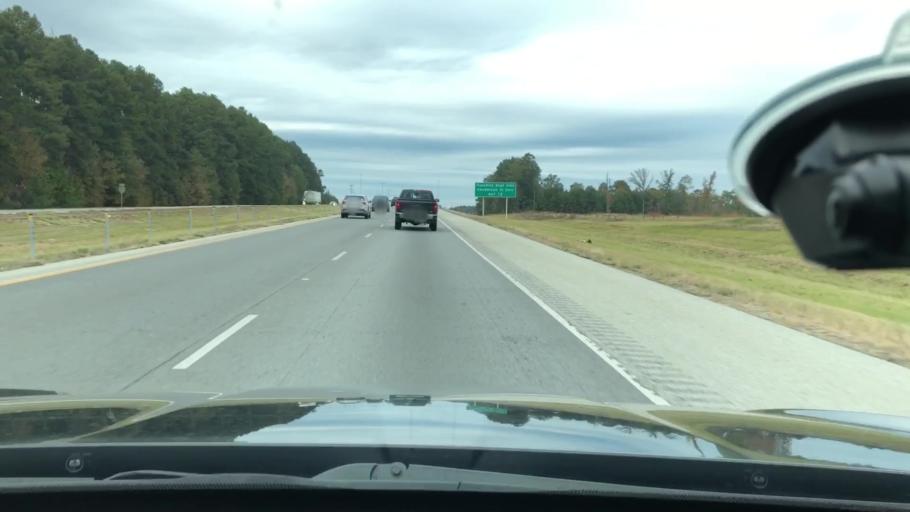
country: US
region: Arkansas
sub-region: Clark County
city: Arkadelphia
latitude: 34.1098
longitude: -93.0975
